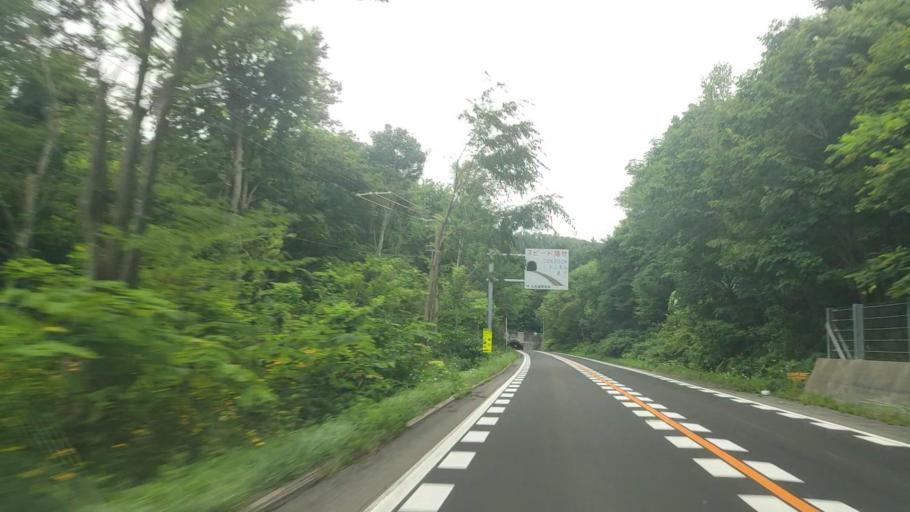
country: JP
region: Hokkaido
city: Niseko Town
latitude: 42.5970
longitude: 140.6032
